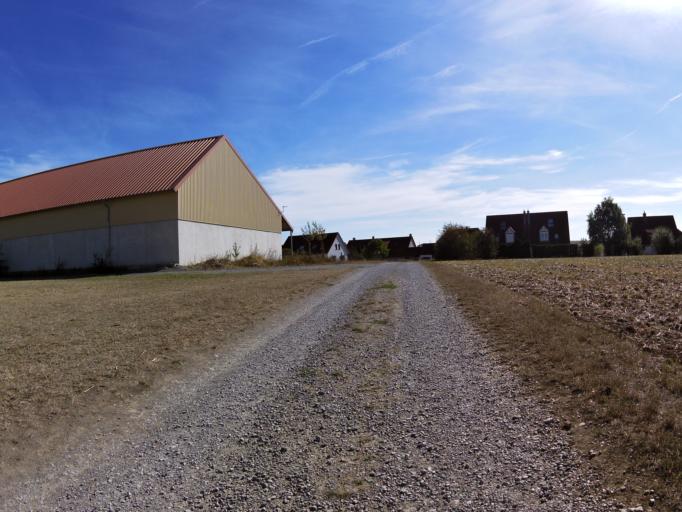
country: DE
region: Bavaria
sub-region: Regierungsbezirk Unterfranken
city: Eisingen
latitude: 49.7638
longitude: 9.8280
